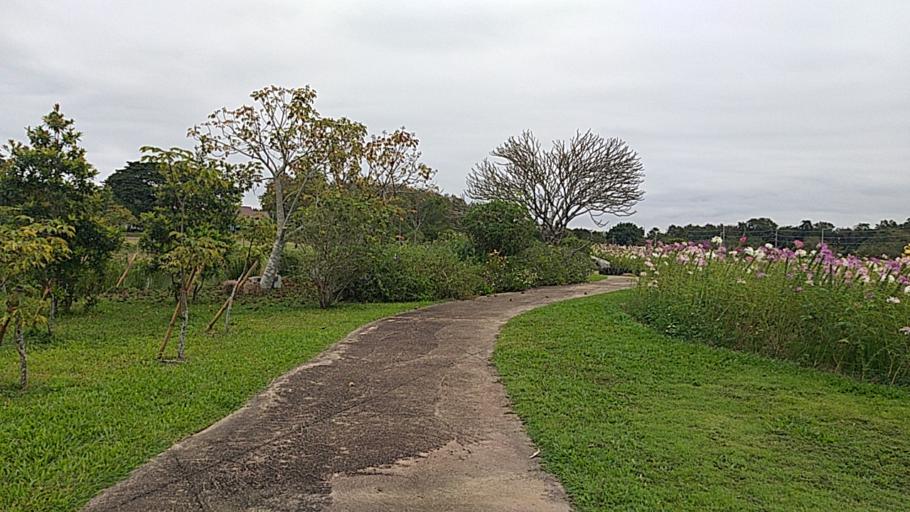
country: TH
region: Chiang Rai
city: Mae Lao
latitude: 19.8541
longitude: 99.7417
